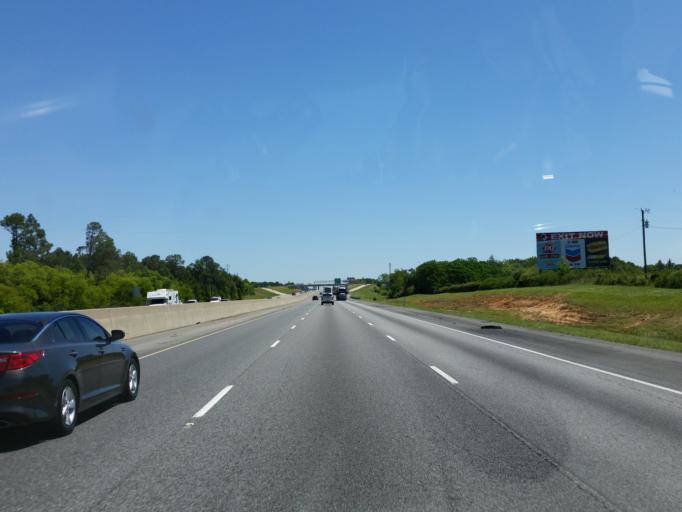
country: US
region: Georgia
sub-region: Turner County
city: Ashburn
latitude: 31.7418
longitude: -83.6564
